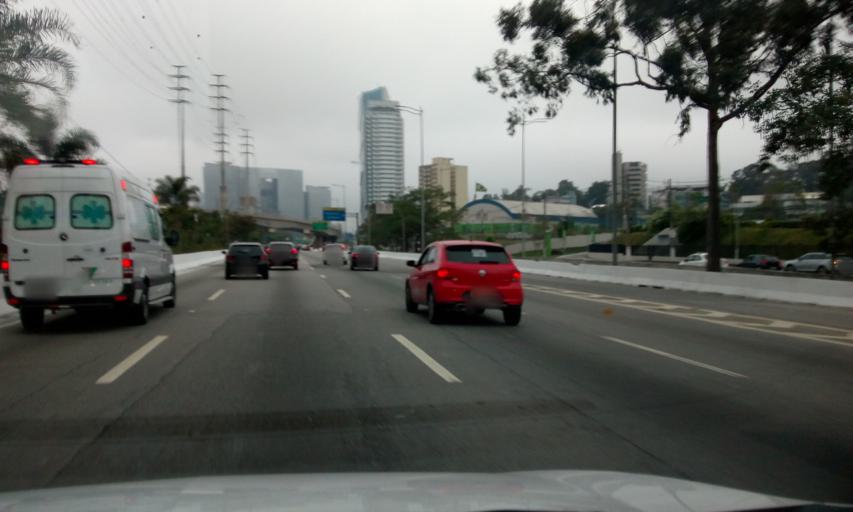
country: BR
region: Sao Paulo
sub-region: Sao Paulo
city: Sao Paulo
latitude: -23.6112
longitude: -46.7003
